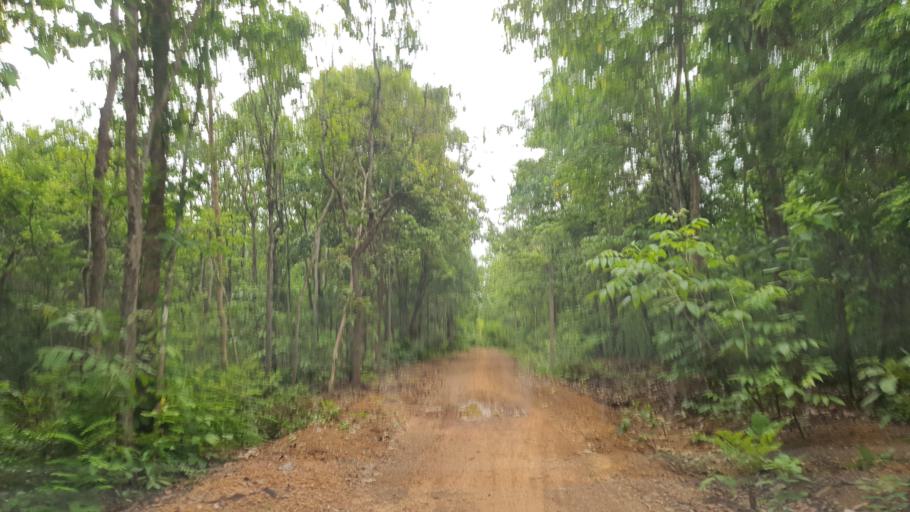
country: TH
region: Sukhothai
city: Thung Saliam
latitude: 17.2406
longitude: 99.5436
